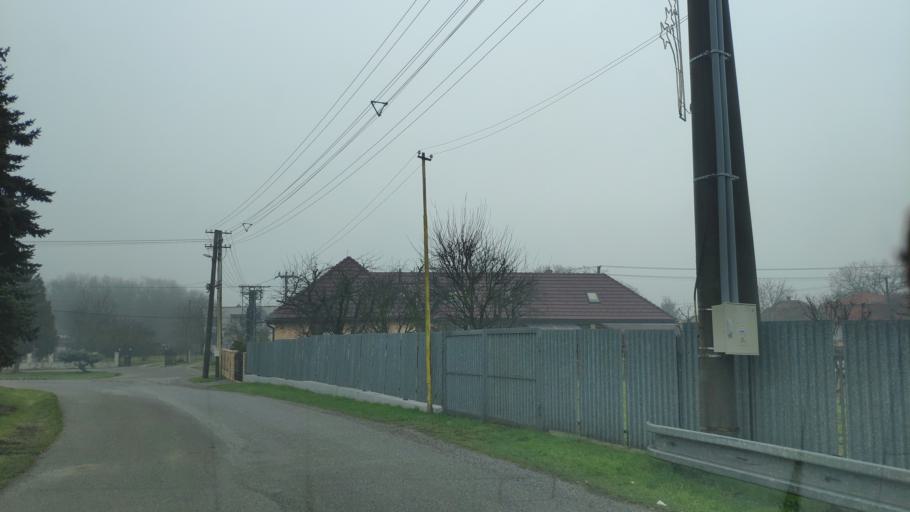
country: SK
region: Kosicky
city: Kosice
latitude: 48.7080
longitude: 21.3302
